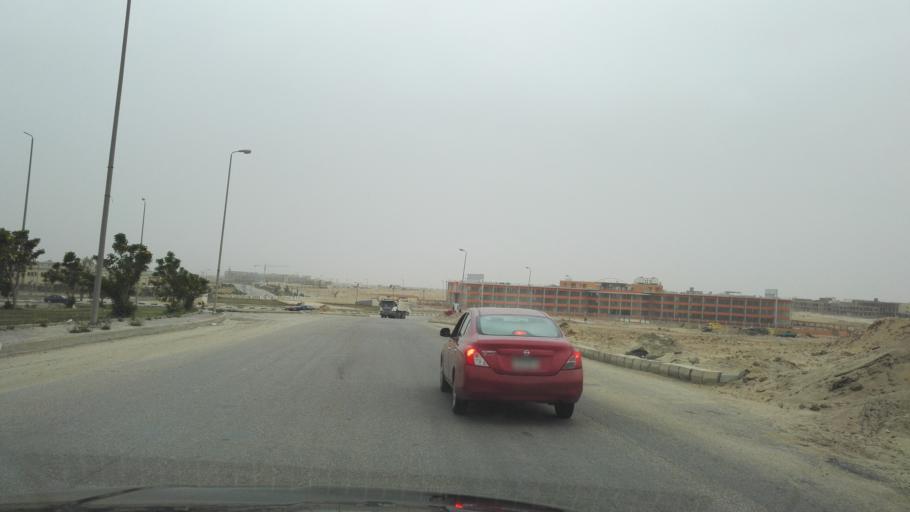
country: EG
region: Muhafazat al Qalyubiyah
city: Al Khankah
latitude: 30.0408
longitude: 31.5255
